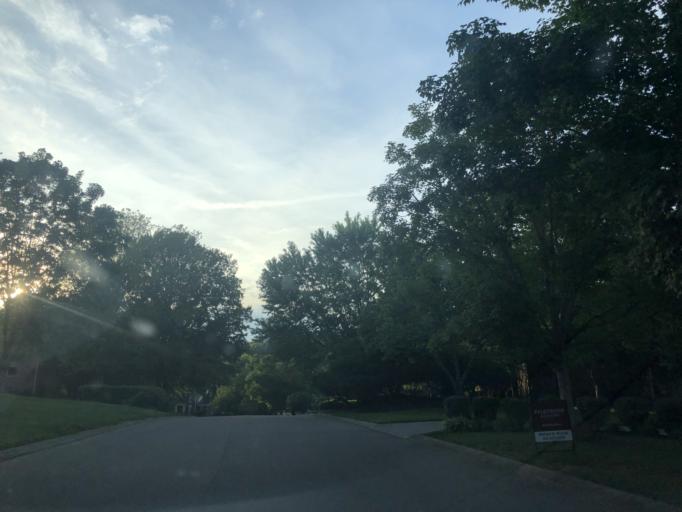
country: US
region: Tennessee
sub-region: Davidson County
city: Belle Meade
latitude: 36.0513
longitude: -86.9214
